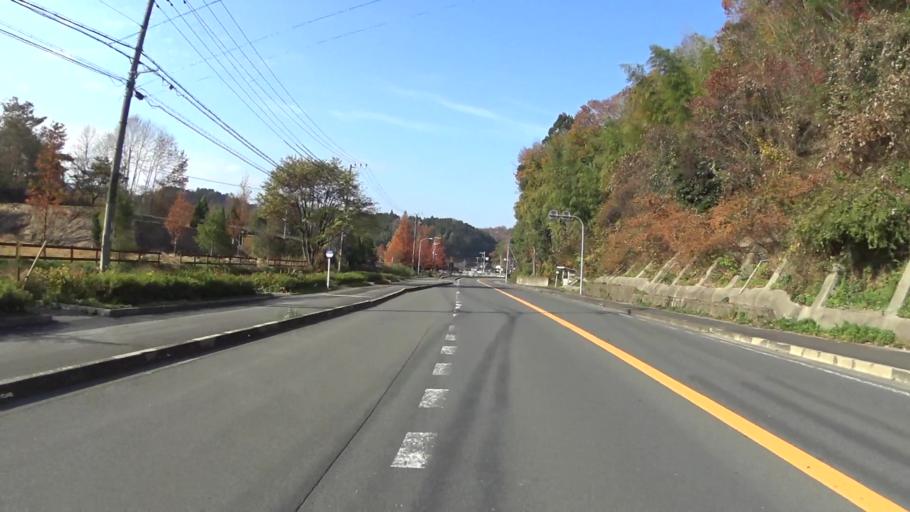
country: JP
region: Kyoto
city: Ayabe
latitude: 35.1794
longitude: 135.3509
